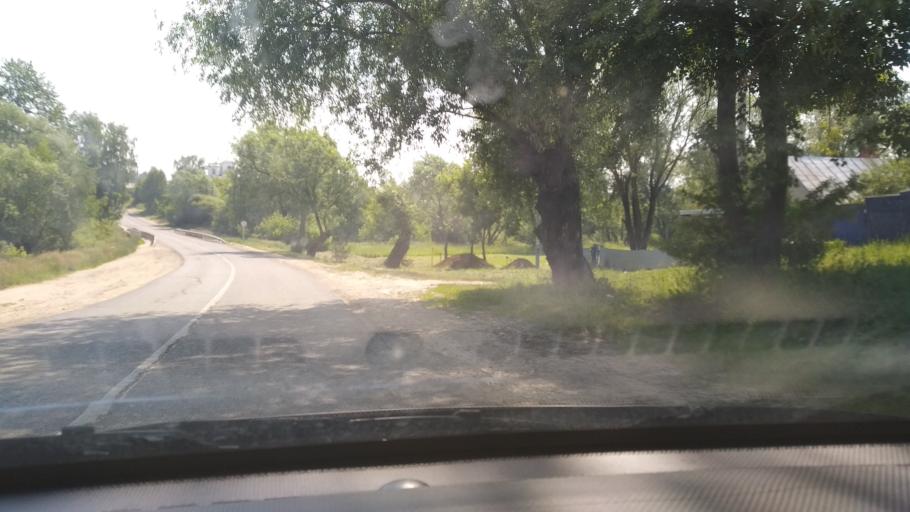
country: RU
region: Tatarstan
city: Osinovo
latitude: 55.9820
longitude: 48.7979
